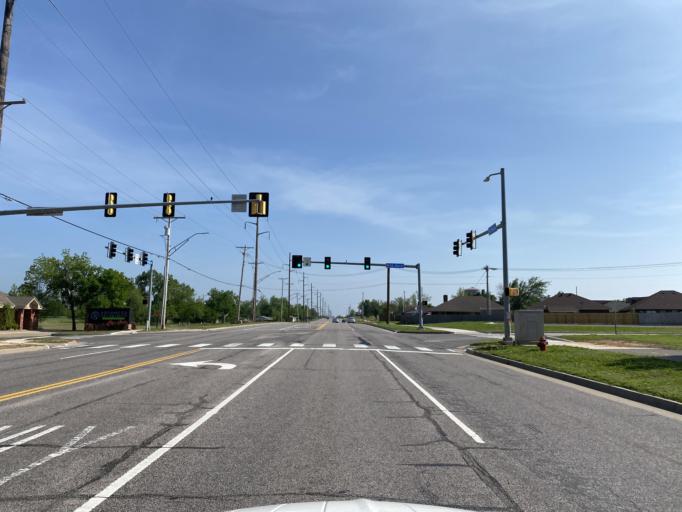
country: US
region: Oklahoma
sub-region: Oklahoma County
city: Midwest City
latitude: 35.4424
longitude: -97.3532
